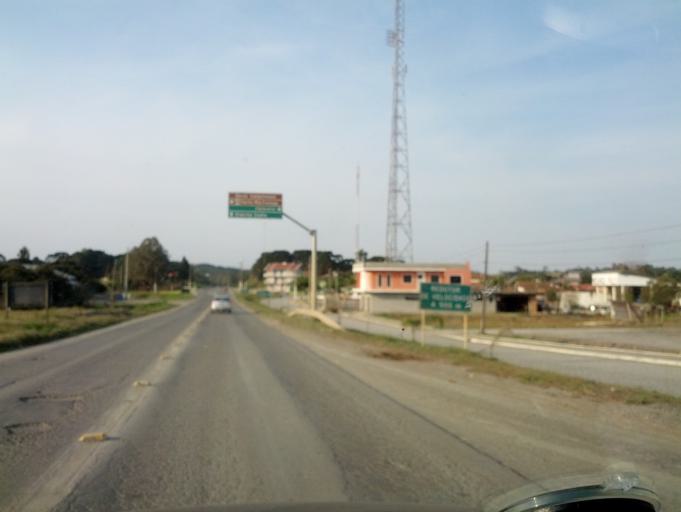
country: BR
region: Santa Catarina
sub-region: Otacilio Costa
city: Otacilio Costa
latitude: -27.5807
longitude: -50.1615
